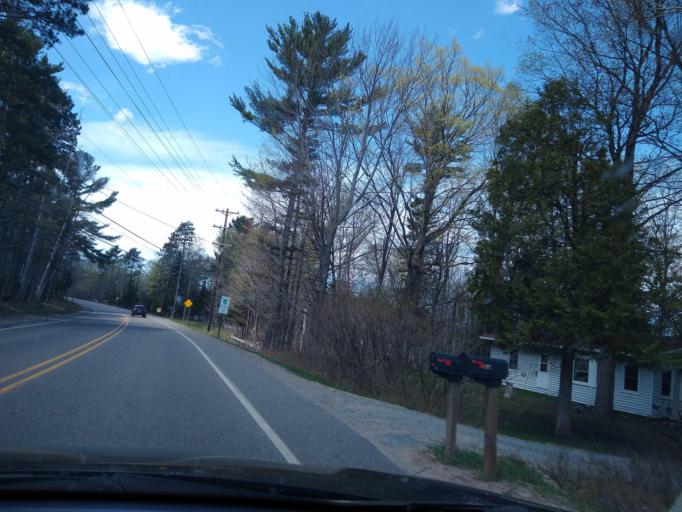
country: US
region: Michigan
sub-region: Marquette County
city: Trowbridge Park
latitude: 46.5825
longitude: -87.4313
